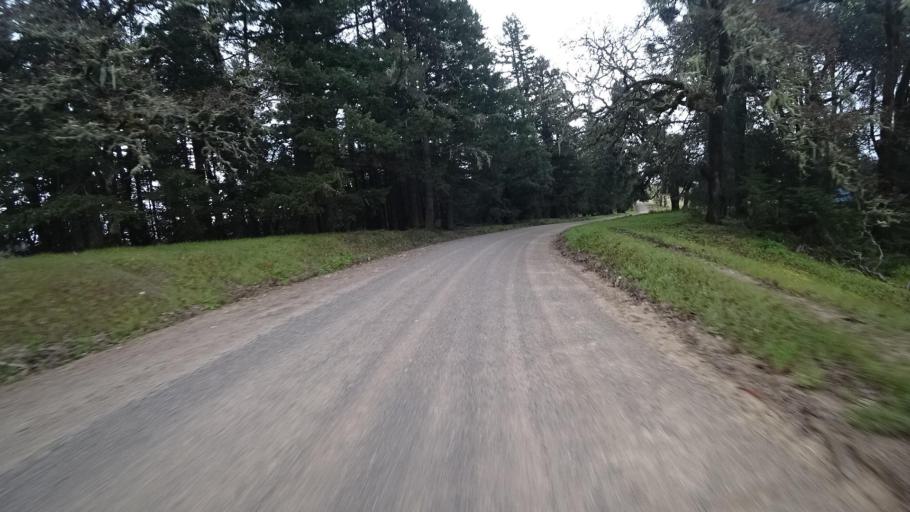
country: US
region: California
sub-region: Humboldt County
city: Redway
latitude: 40.2108
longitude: -123.7319
